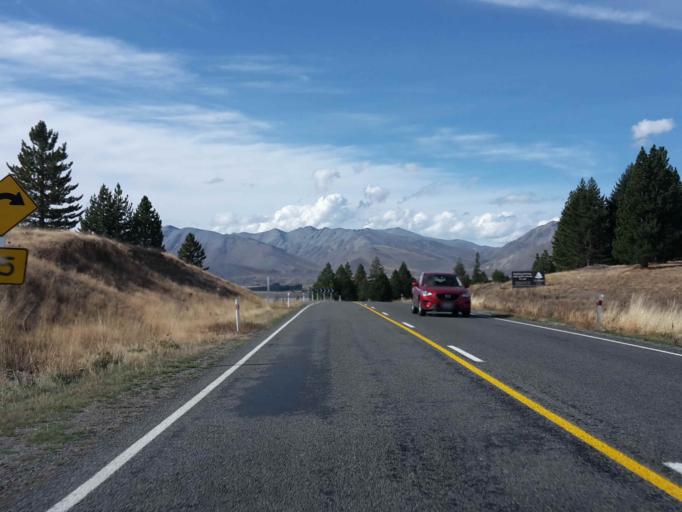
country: NZ
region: Canterbury
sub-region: Timaru District
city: Pleasant Point
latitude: -44.0013
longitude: 170.4578
